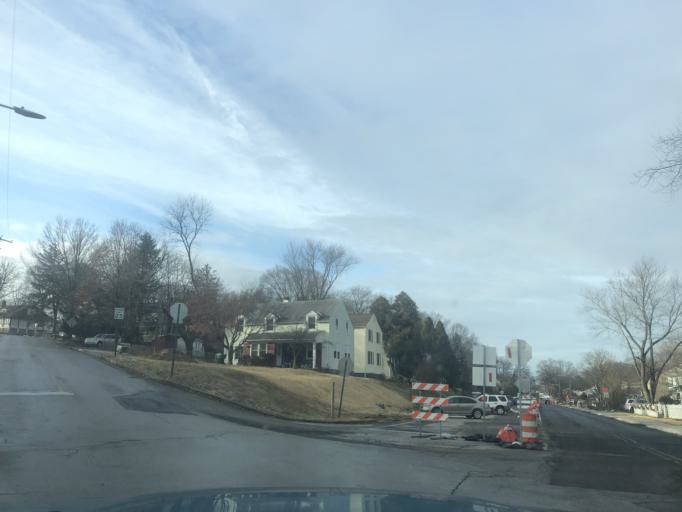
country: US
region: Pennsylvania
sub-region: Montgomery County
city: Glenside
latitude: 40.1193
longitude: -75.1374
